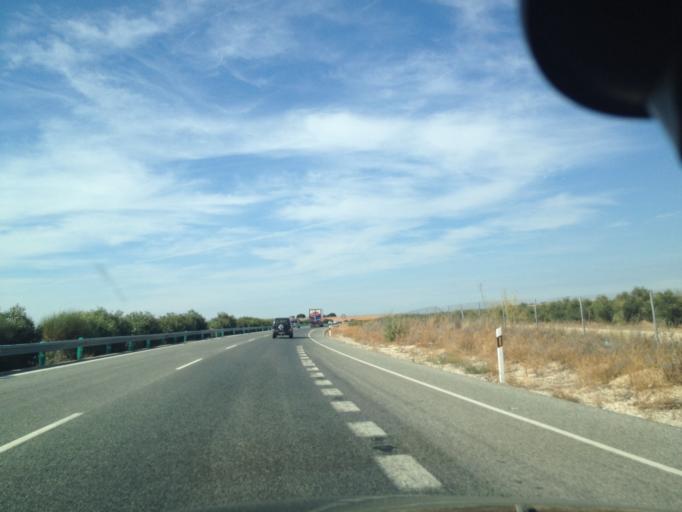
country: ES
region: Andalusia
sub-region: Provincia de Sevilla
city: Osuna
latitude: 37.2325
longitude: -5.1676
